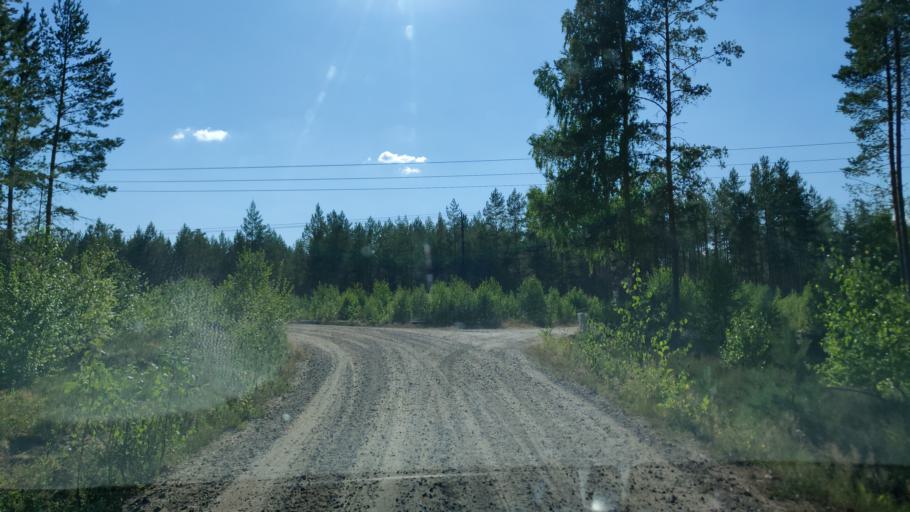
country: SE
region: Vaermland
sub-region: Hagfors Kommun
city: Ekshaerad
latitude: 60.0644
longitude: 13.5209
